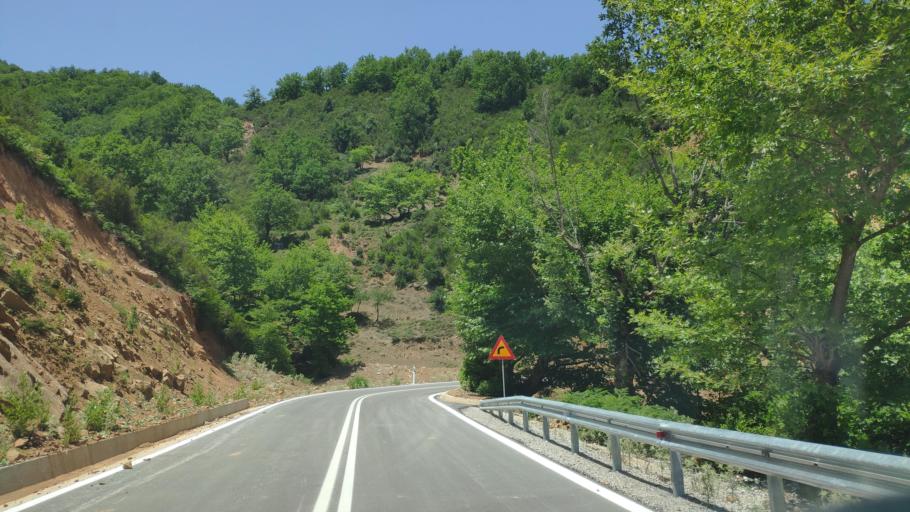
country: GR
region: Epirus
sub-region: Nomos Artas
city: Ano Kalentini
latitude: 39.1919
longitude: 21.3500
